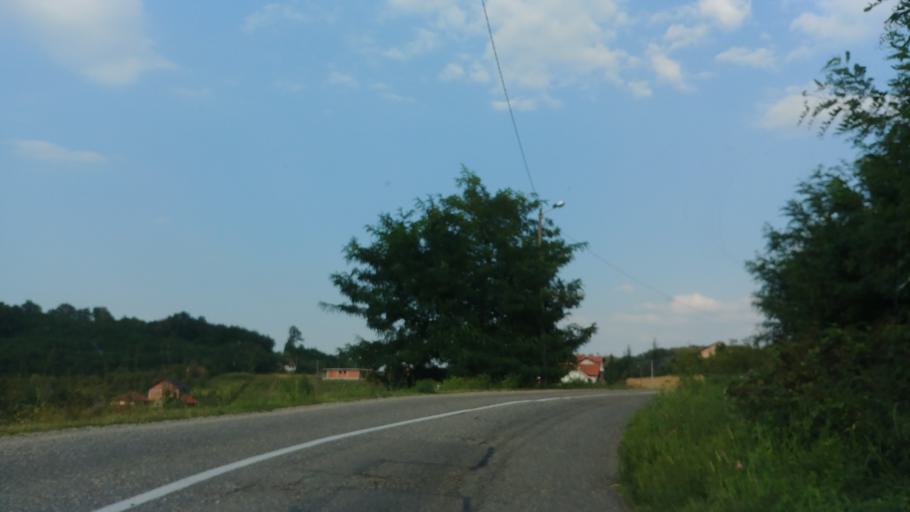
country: BA
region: Republika Srpska
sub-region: Opstina Ugljevik
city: Ugljevik
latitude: 44.7072
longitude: 18.9492
